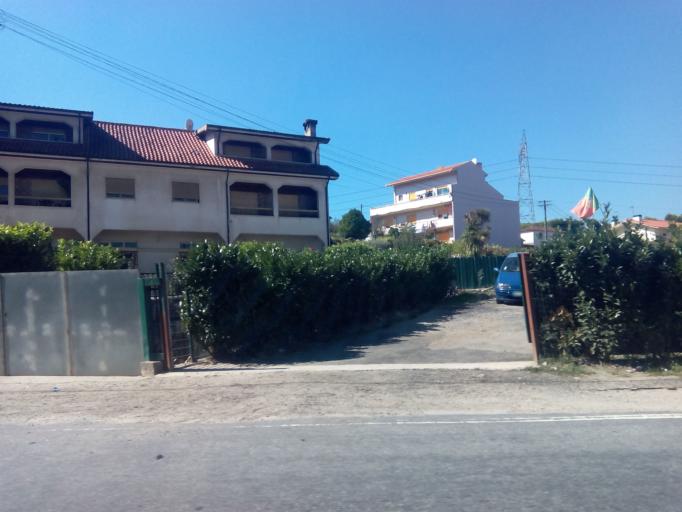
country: PT
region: Porto
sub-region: Paredes
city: Gandra
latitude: 41.1937
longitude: -8.4363
